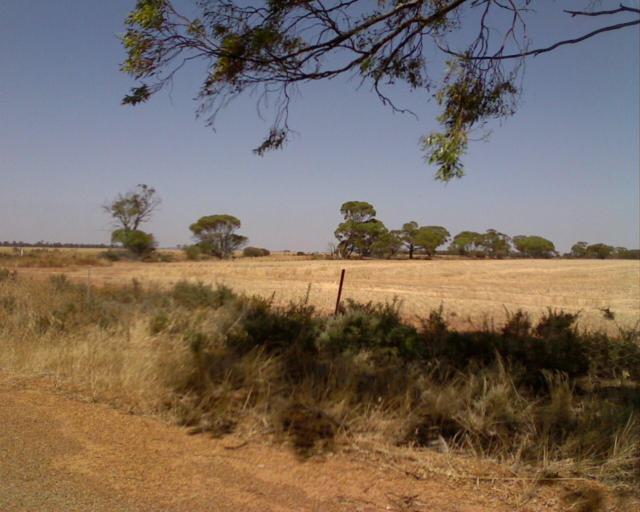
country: AU
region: Western Australia
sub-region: Merredin
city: Merredin
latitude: -30.7655
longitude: 118.2092
